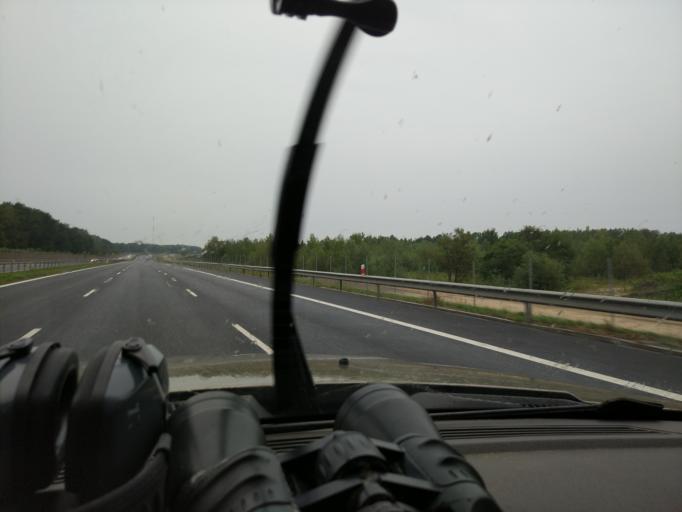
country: PL
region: Masovian Voivodeship
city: Zielonka
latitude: 52.3371
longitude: 21.1568
